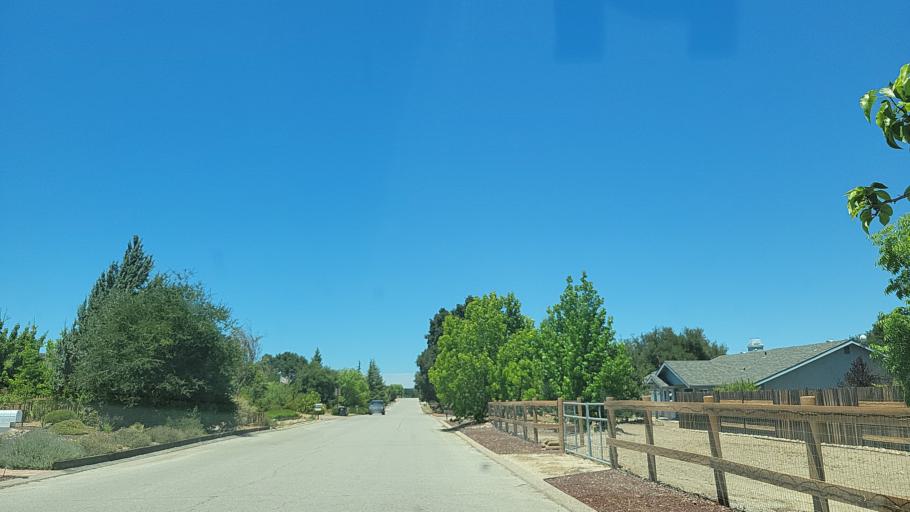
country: US
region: California
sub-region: San Luis Obispo County
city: Atascadero
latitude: 35.5189
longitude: -120.6835
